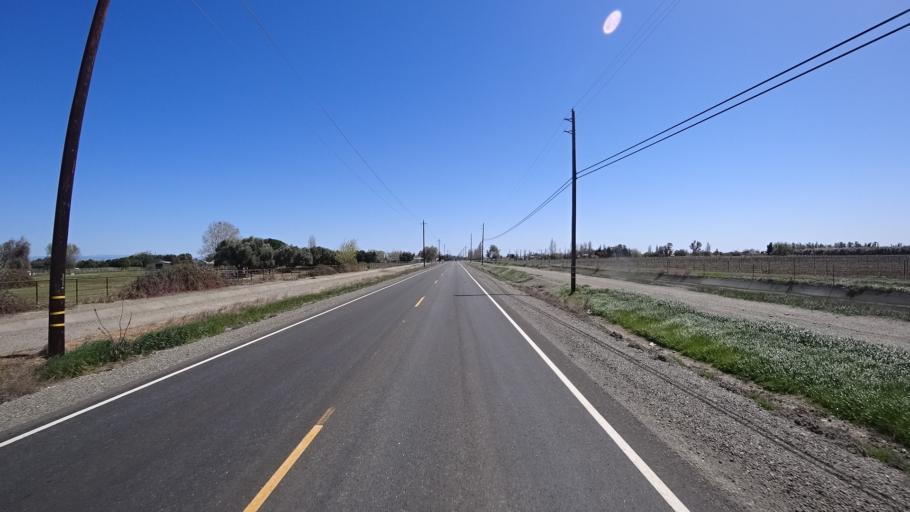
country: US
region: California
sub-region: Glenn County
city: Orland
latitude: 39.7648
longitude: -122.2421
